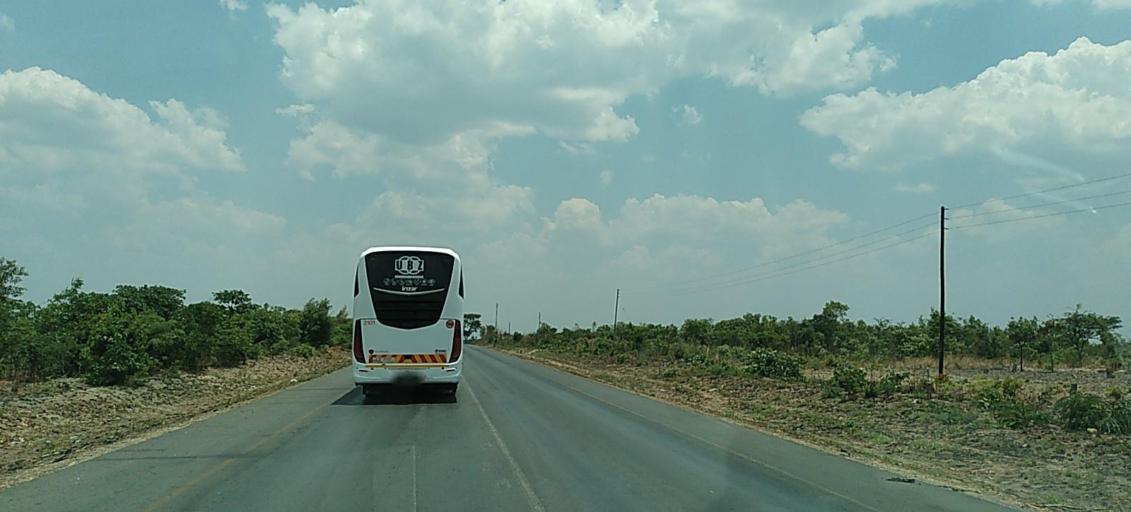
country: ZM
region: Central
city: Kapiri Mposhi
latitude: -14.0580
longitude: 28.6463
